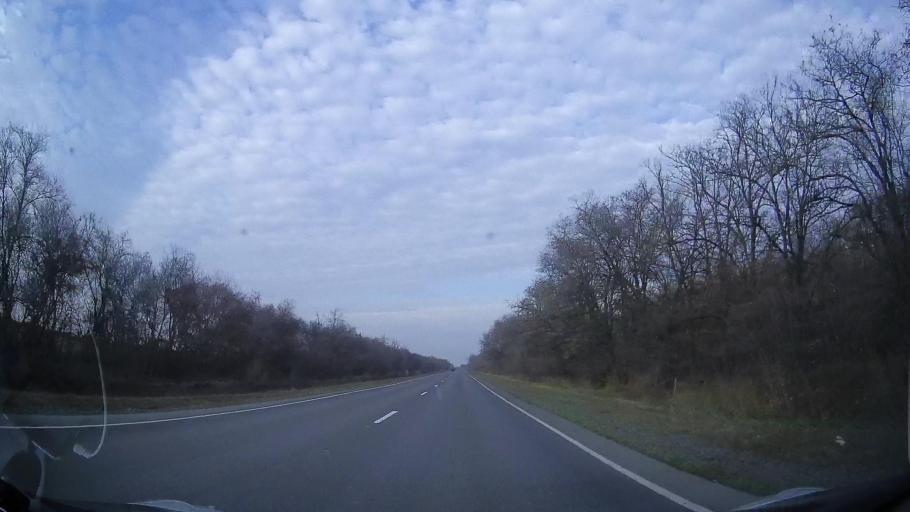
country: RU
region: Rostov
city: Bagayevskaya
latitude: 47.1278
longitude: 40.2767
